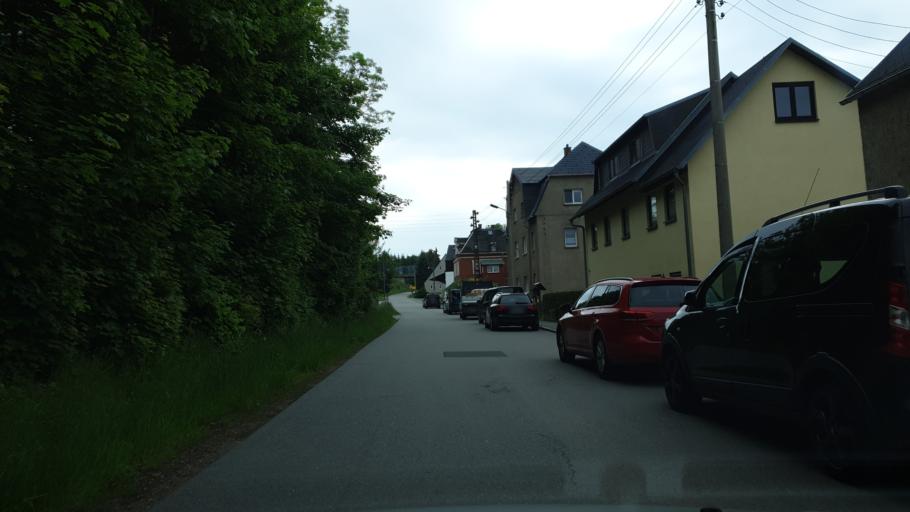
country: DE
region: Saxony
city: Stollberg
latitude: 50.7001
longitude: 12.7742
